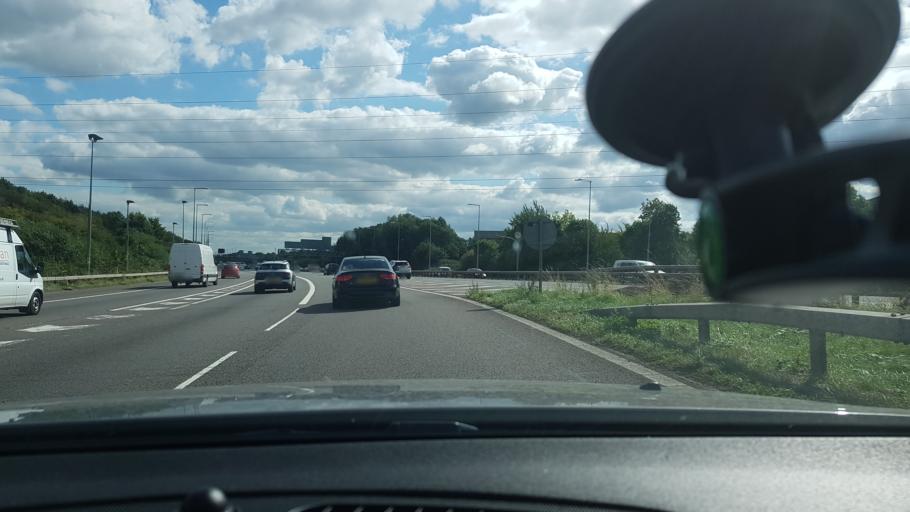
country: GB
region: England
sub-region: South Gloucestershire
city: Almondsbury
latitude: 51.5484
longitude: -2.5495
